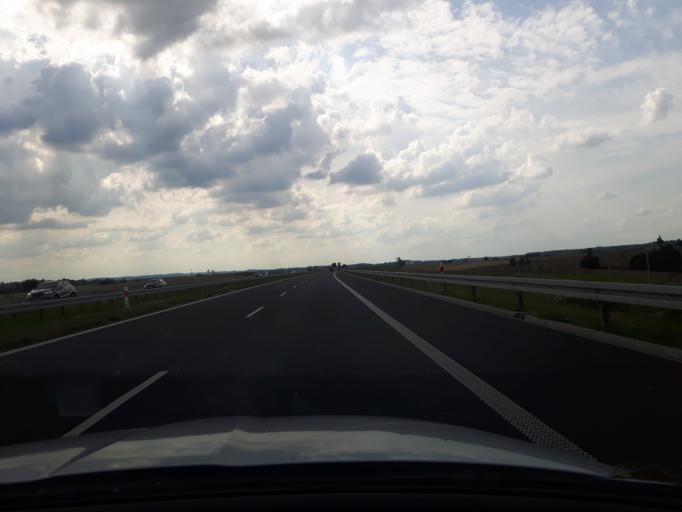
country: PL
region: Warmian-Masurian Voivodeship
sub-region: Powiat ostrodzki
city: Gierzwald
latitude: 53.5922
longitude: 20.1135
